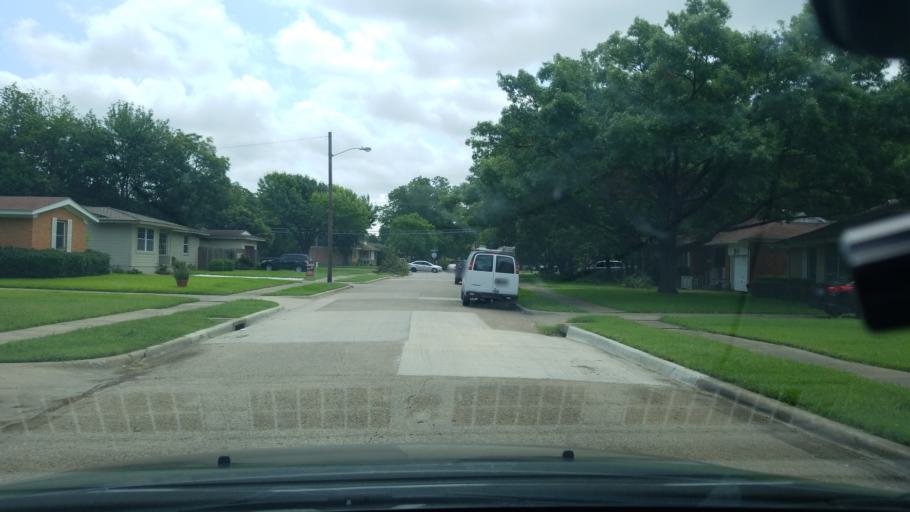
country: US
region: Texas
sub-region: Dallas County
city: Garland
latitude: 32.8290
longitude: -96.6768
